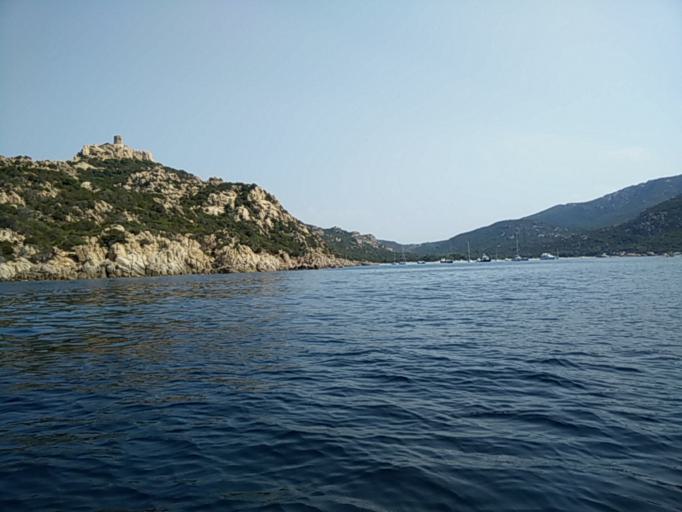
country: FR
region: Corsica
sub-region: Departement de la Corse-du-Sud
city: Sartene
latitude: 41.4899
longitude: 8.9284
